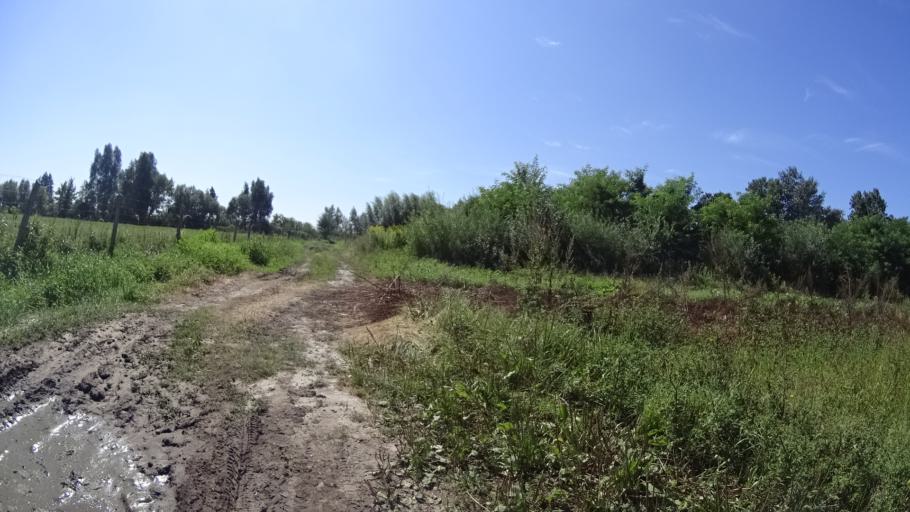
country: PL
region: Masovian Voivodeship
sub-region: Powiat grojecki
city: Goszczyn
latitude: 51.6642
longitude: 20.8770
